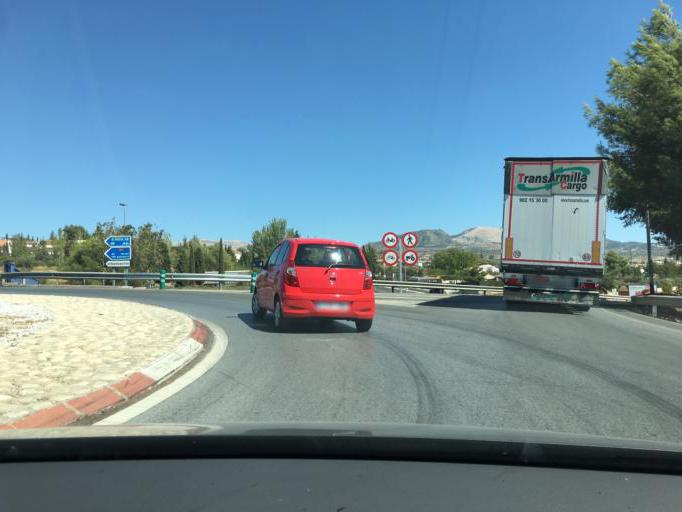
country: ES
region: Andalusia
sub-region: Provincia de Granada
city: Albolote
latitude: 37.2363
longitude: -3.6468
